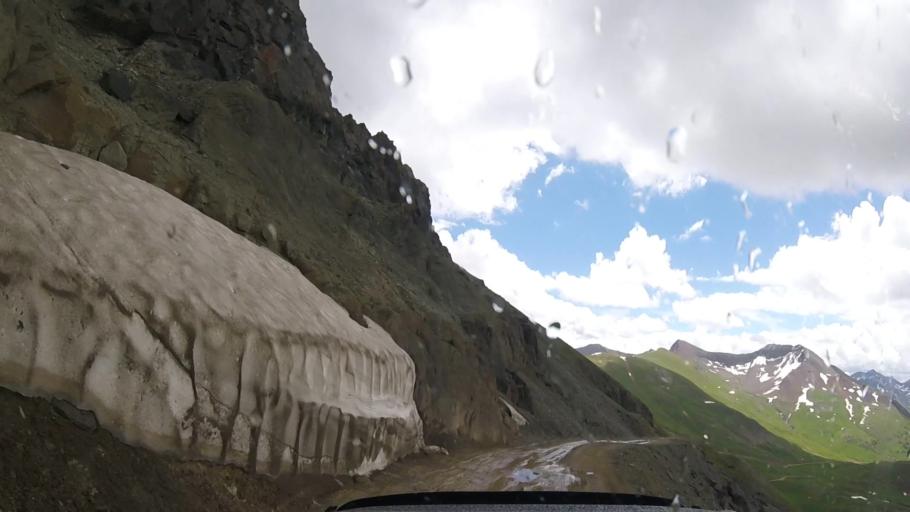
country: US
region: Colorado
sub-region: Ouray County
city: Ouray
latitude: 37.9674
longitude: -107.5877
